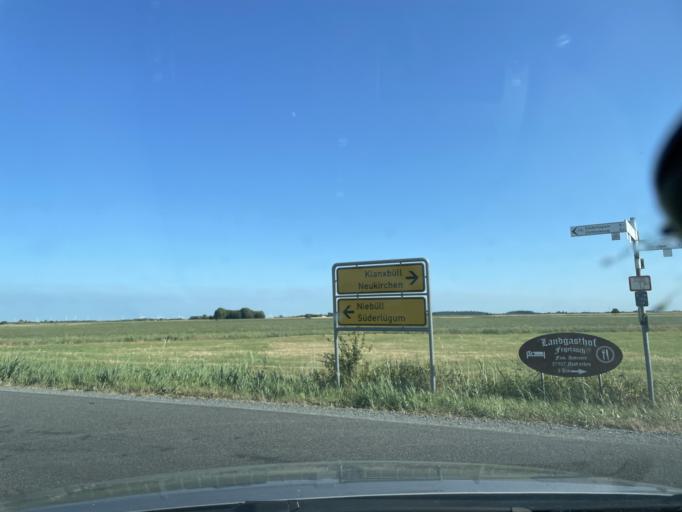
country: DE
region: Schleswig-Holstein
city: Neukirchen
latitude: 54.8786
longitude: 8.7755
